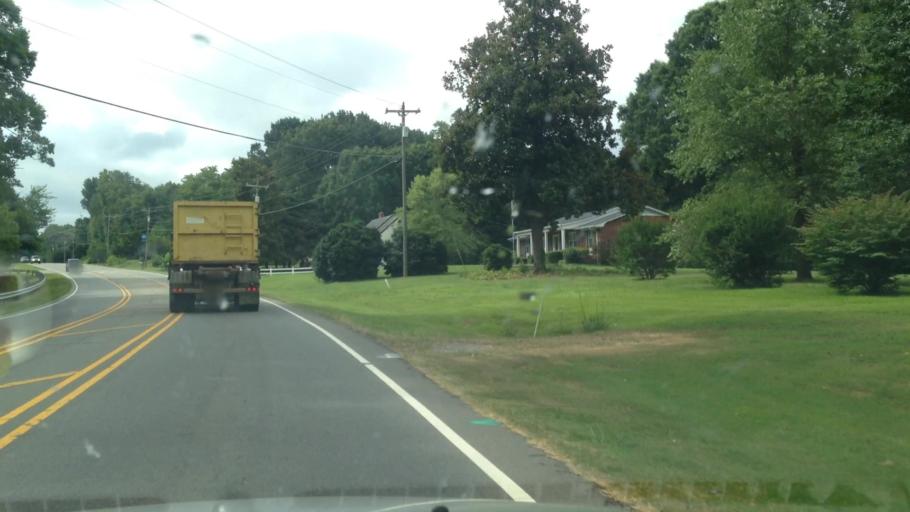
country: US
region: North Carolina
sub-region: Rockingham County
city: Wentworth
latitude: 36.3959
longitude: -79.7579
